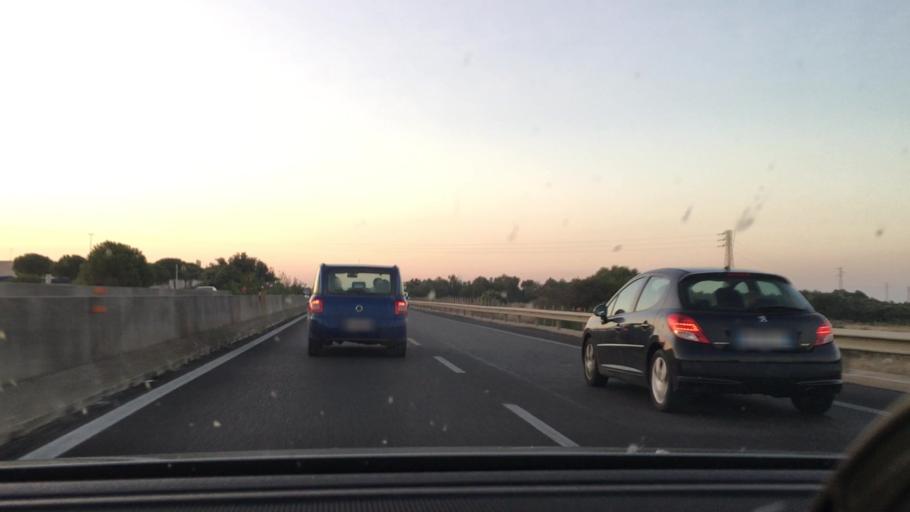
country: IT
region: Apulia
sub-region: Provincia di Lecce
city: Surbo
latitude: 40.3947
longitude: 18.1177
